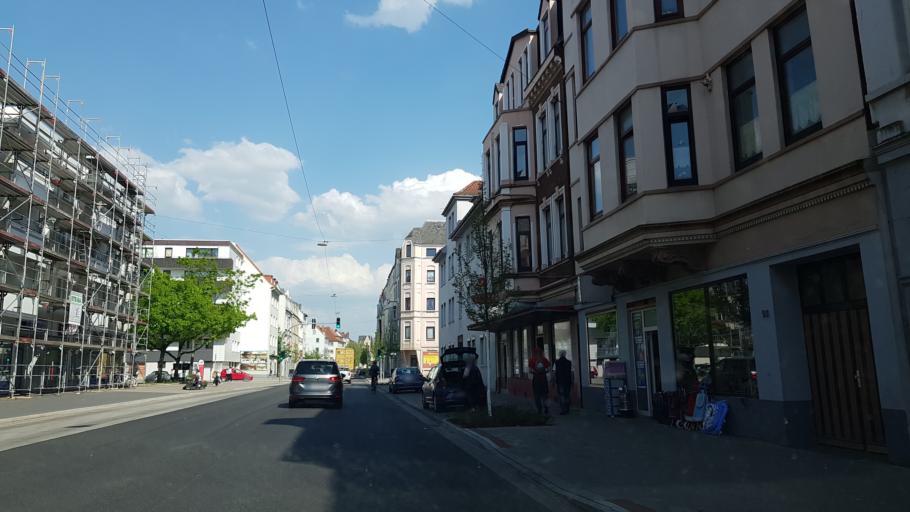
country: DE
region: Bremen
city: Bremerhaven
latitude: 53.5607
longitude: 8.5793
